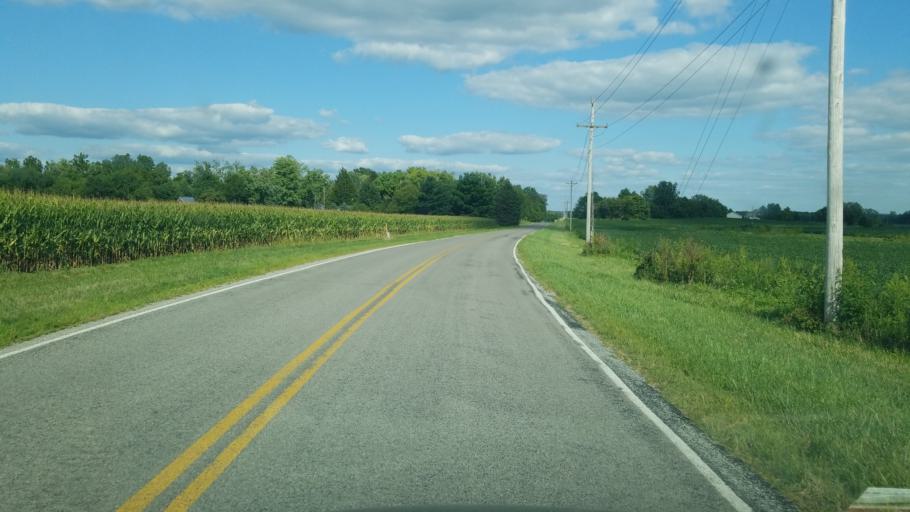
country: US
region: Ohio
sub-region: Champaign County
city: Urbana
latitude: 40.1319
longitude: -83.8426
